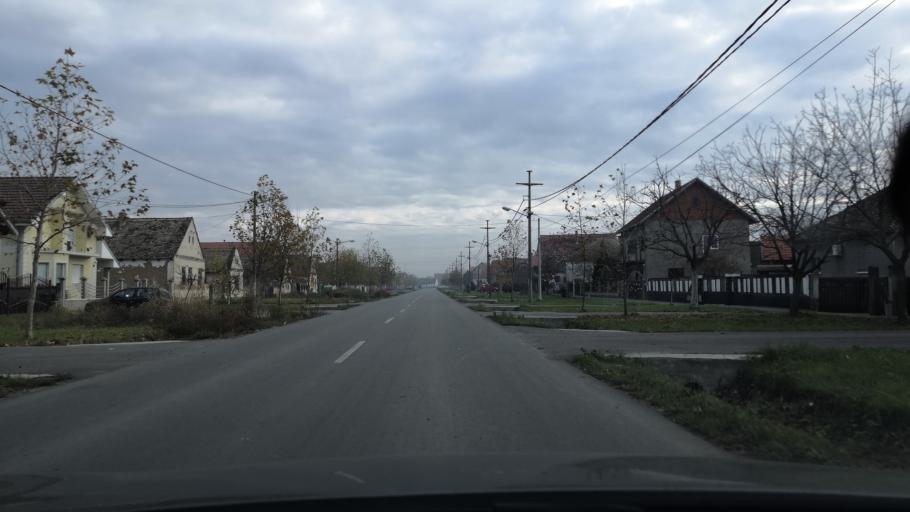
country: RS
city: Ugrinovci
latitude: 44.8791
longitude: 20.1745
